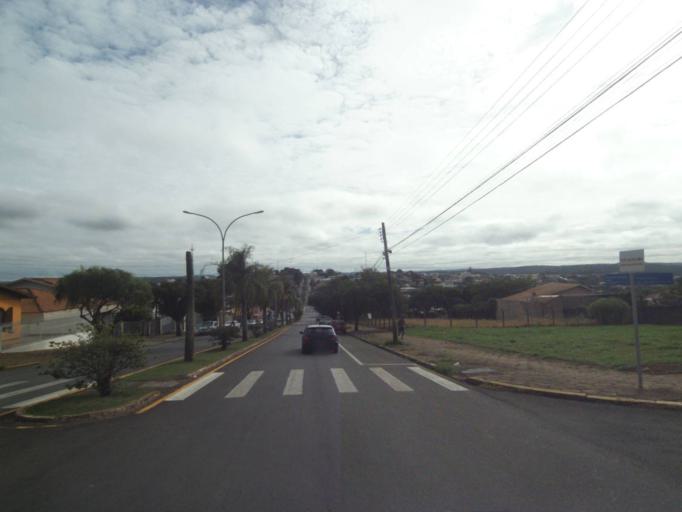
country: BR
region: Parana
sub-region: Telemaco Borba
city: Telemaco Borba
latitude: -24.3353
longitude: -50.6269
